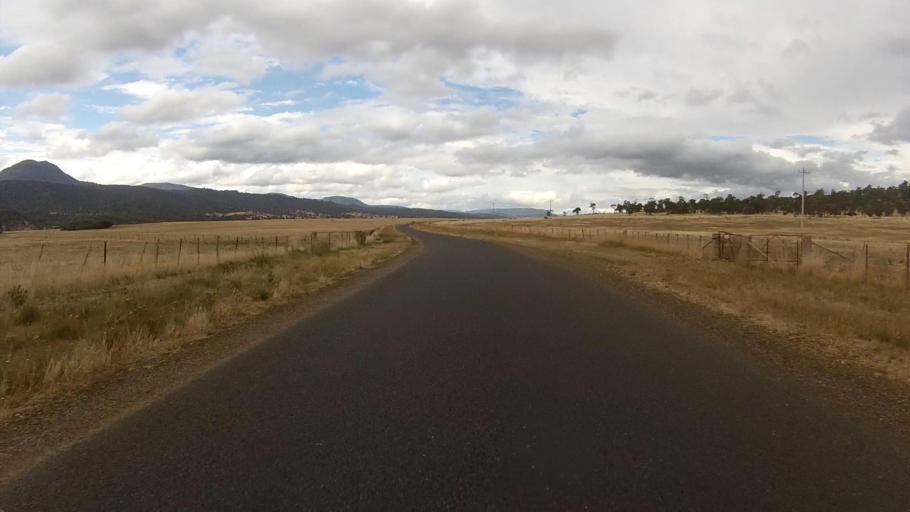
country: AU
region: Tasmania
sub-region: Northern Midlands
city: Evandale
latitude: -41.8265
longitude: 147.7914
